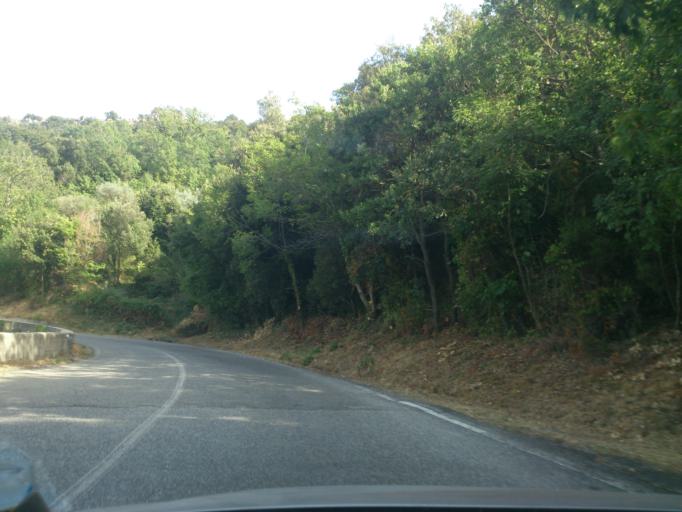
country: IT
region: Calabria
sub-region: Provincia di Reggio Calabria
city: Pazzano
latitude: 38.4681
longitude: 16.4363
